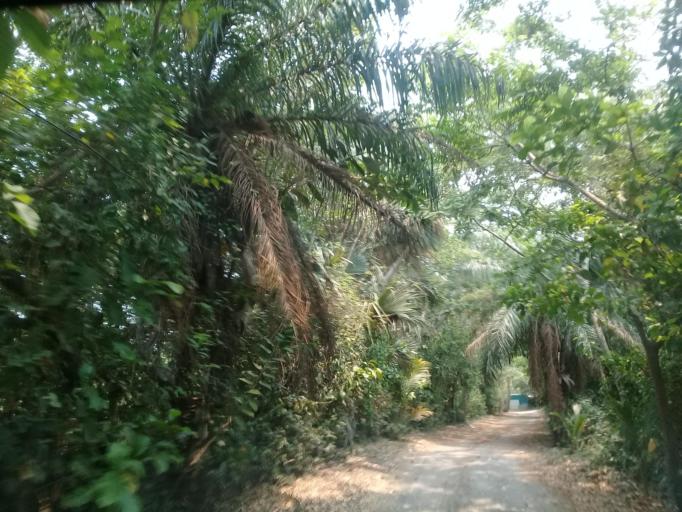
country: MX
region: Veracruz
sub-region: Veracruz
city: Hacienda Sotavento
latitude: 19.1385
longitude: -96.1586
